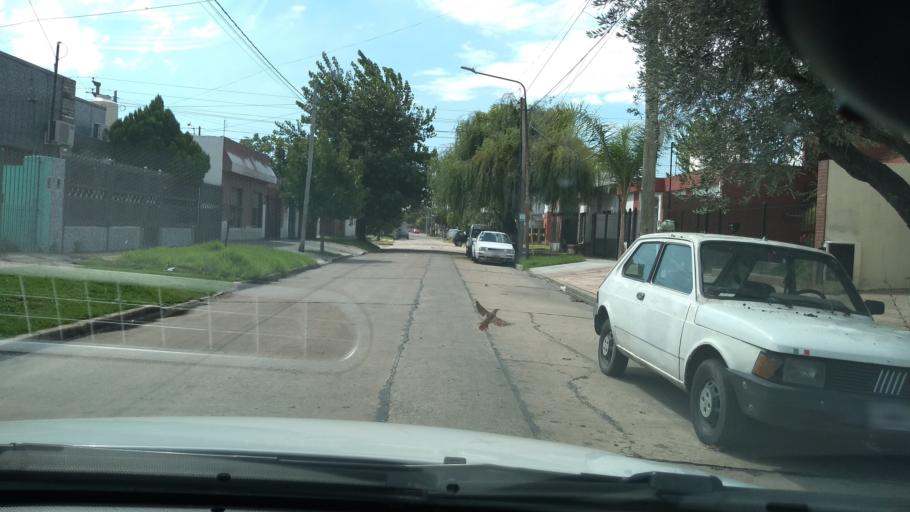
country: AR
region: Buenos Aires
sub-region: Partido de Moron
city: Moron
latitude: -34.6663
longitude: -58.6060
